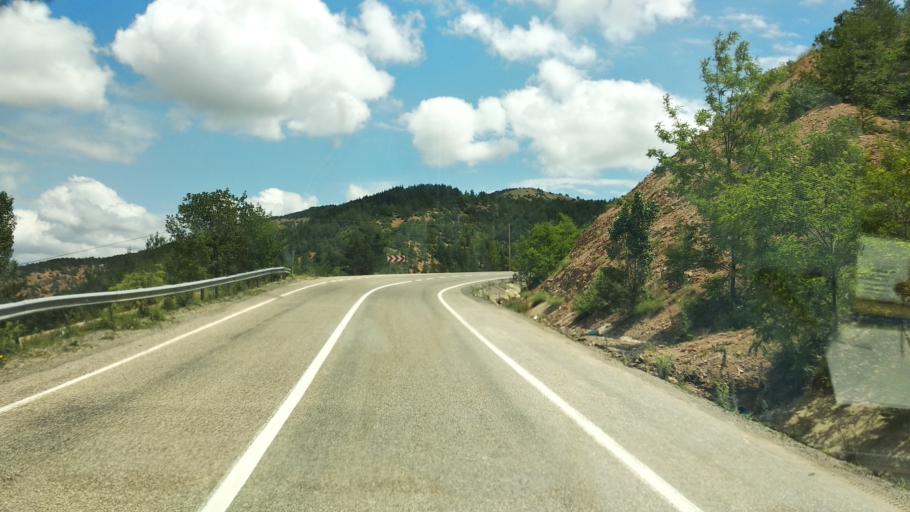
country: TR
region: Gumushane
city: Kose
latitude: 40.3009
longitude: 39.5555
